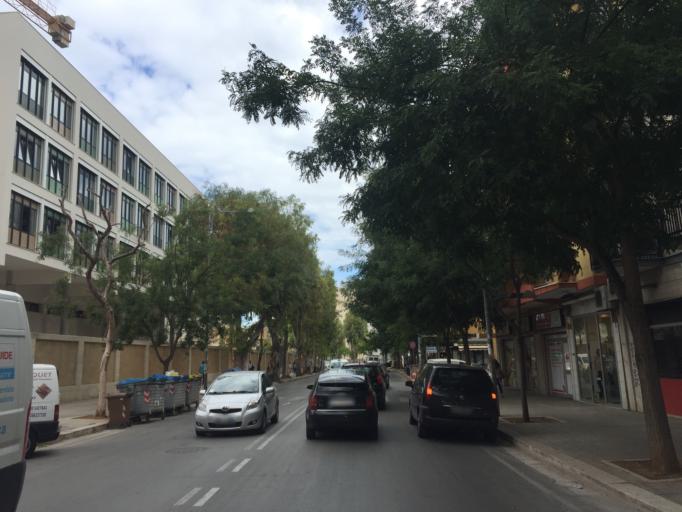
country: IT
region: Apulia
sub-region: Provincia di Bari
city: Bari
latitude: 41.1101
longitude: 16.8612
